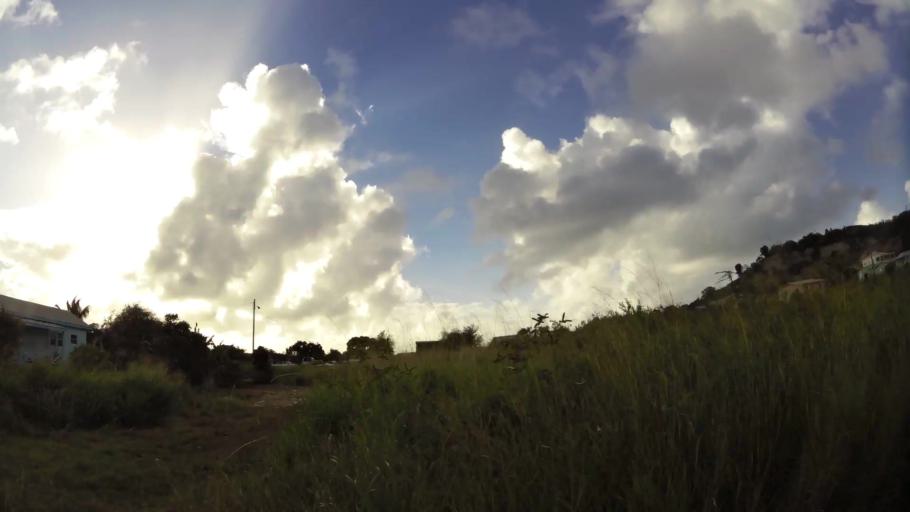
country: AG
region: Saint George
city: Piggotts
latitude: 17.1594
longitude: -61.8205
